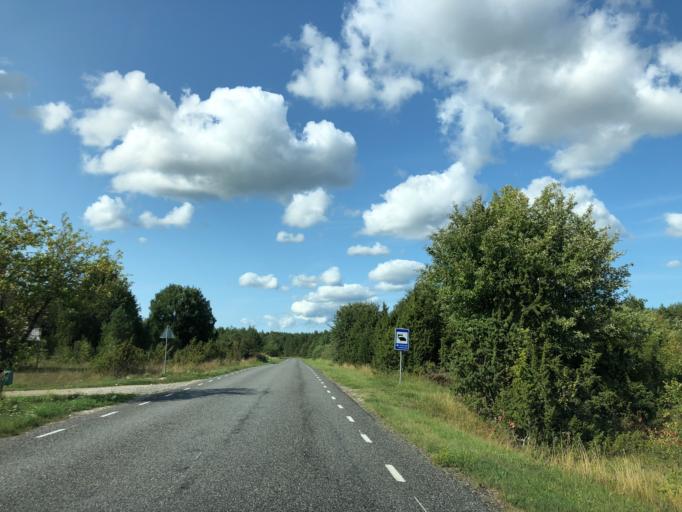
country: EE
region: Hiiumaa
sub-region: Kaerdla linn
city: Kardla
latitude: 58.8032
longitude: 22.7462
